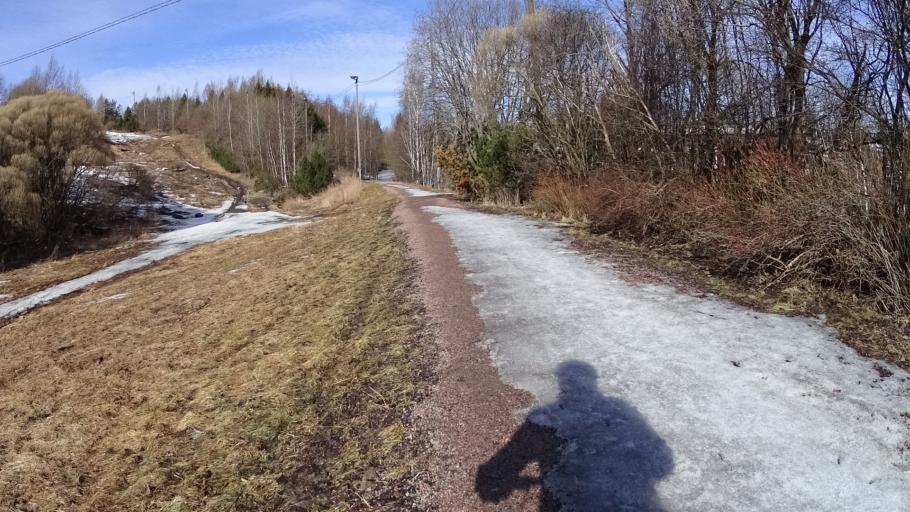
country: FI
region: Uusimaa
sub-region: Helsinki
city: Teekkarikylae
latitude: 60.2513
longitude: 24.8477
